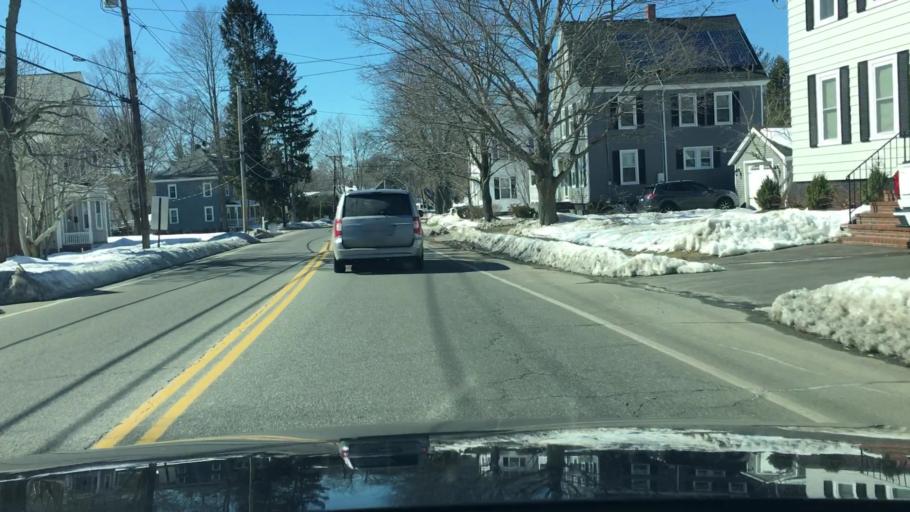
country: US
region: Massachusetts
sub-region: Essex County
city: Amesbury
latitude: 42.8518
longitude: -70.9134
